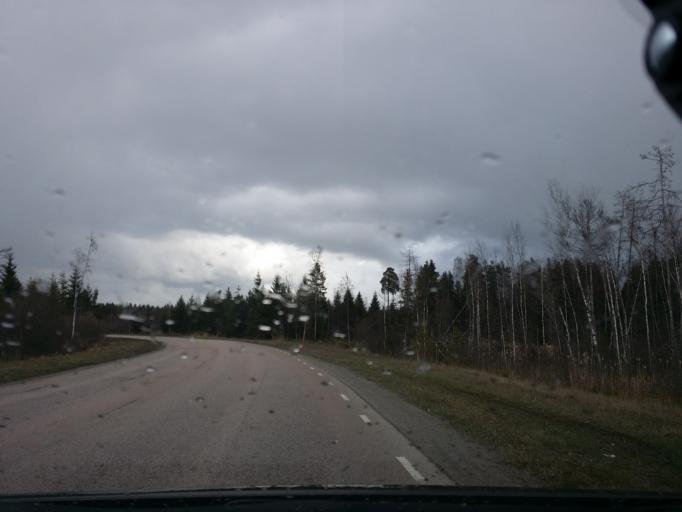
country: SE
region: Uppsala
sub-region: Enkopings Kommun
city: Enkoping
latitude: 59.6288
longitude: 17.1406
